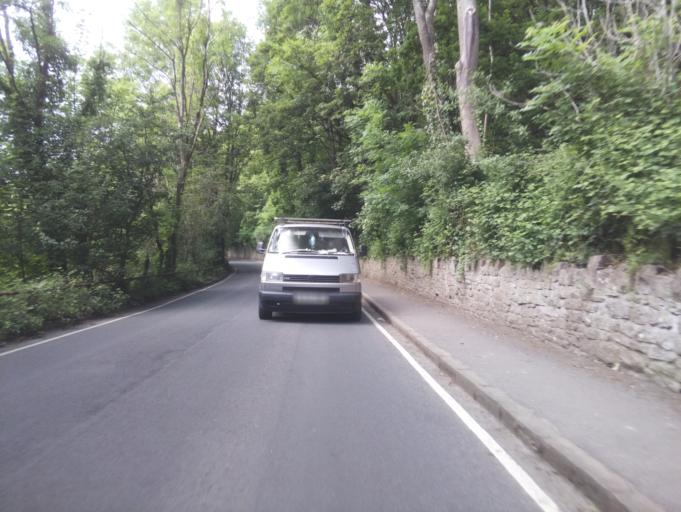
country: GB
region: England
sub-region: South Gloucestershire
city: Kingswood
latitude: 51.4482
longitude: -2.5340
